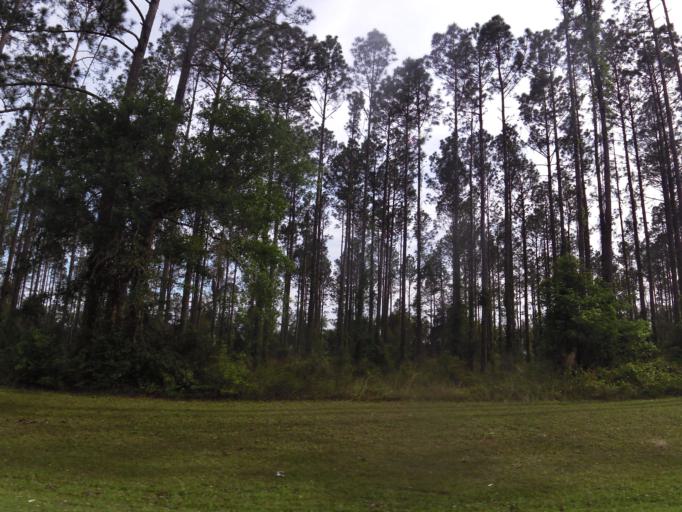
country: US
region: Georgia
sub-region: Camden County
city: Kingsland
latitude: 30.6960
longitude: -81.7235
